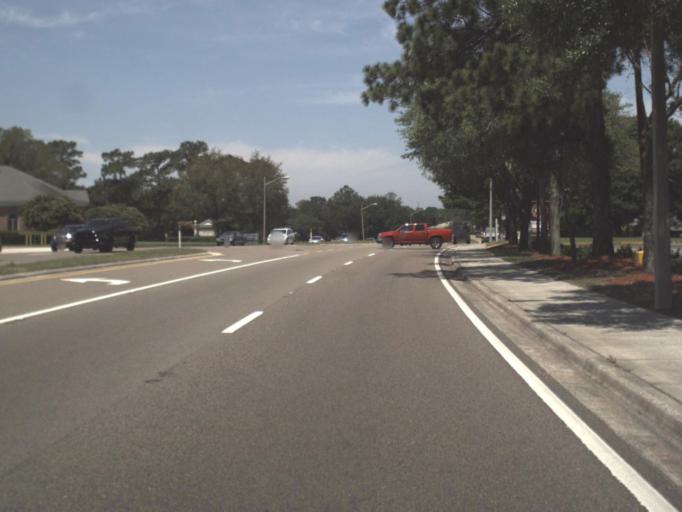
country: US
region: Florida
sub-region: Saint Johns County
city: Fruit Cove
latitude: 30.2191
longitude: -81.5554
